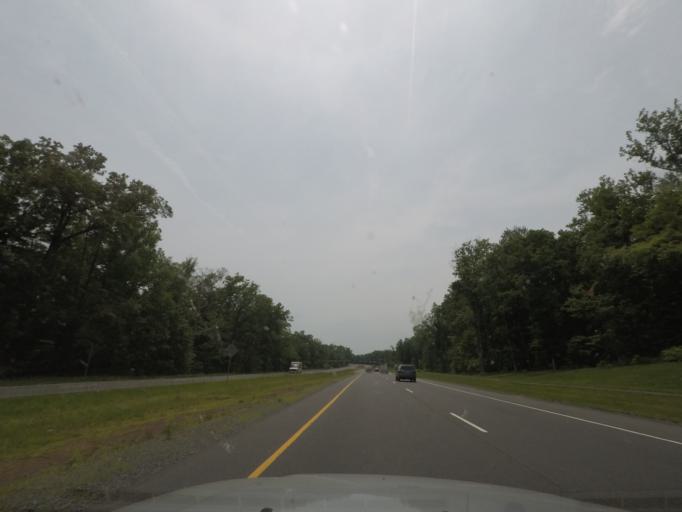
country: US
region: Virginia
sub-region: Prince William County
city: Haymarket
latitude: 38.8091
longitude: -77.6533
